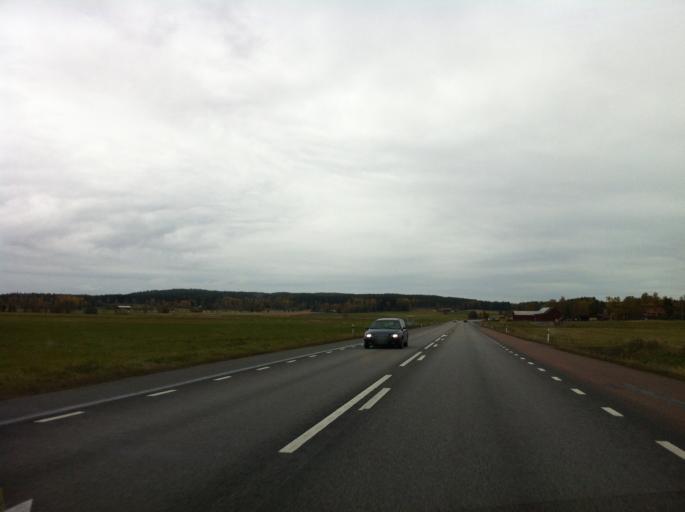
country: SE
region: OErebro
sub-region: Lindesbergs Kommun
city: Stora
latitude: 59.7498
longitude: 15.1440
